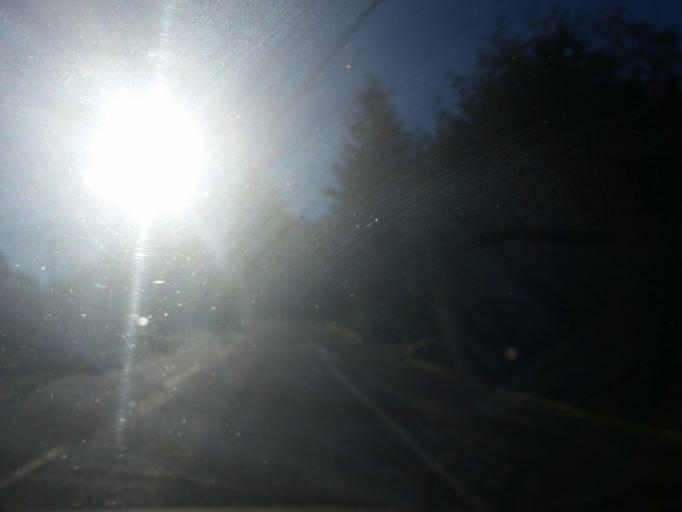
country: US
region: Washington
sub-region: Snohomish County
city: Meadowdale
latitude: 47.8363
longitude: -122.3532
